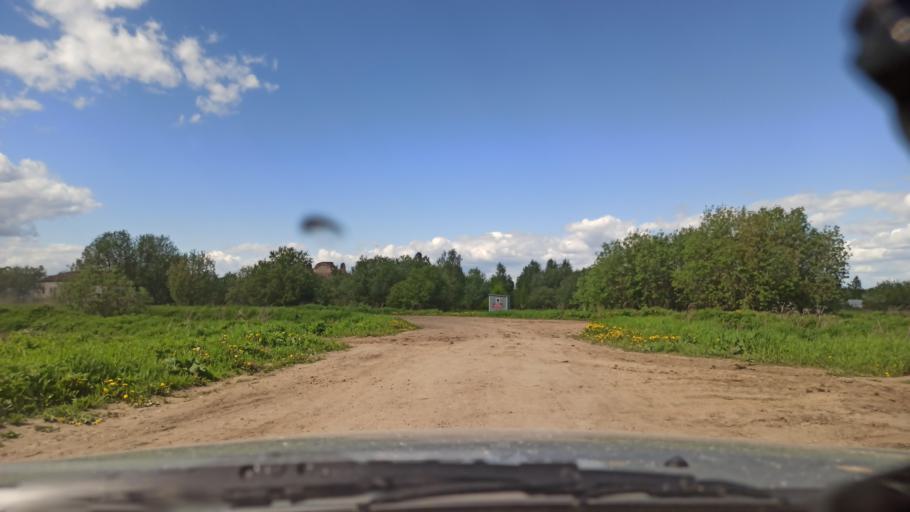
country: RU
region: Vologda
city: Vologda
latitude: 59.3406
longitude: 39.8382
